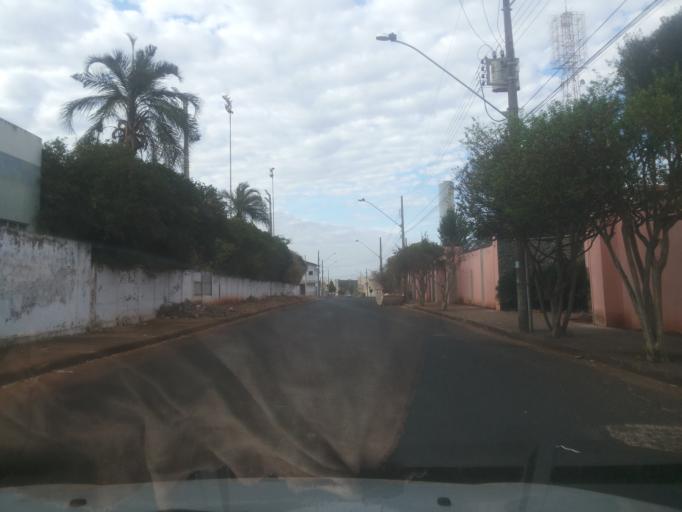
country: BR
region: Minas Gerais
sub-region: Ituiutaba
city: Ituiutaba
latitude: -18.9943
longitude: -49.4571
